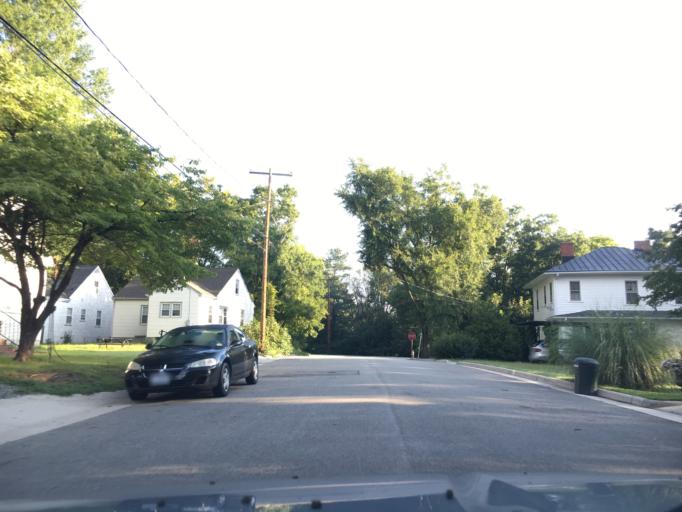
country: US
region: Virginia
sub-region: Halifax County
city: South Boston
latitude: 36.7076
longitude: -78.8954
